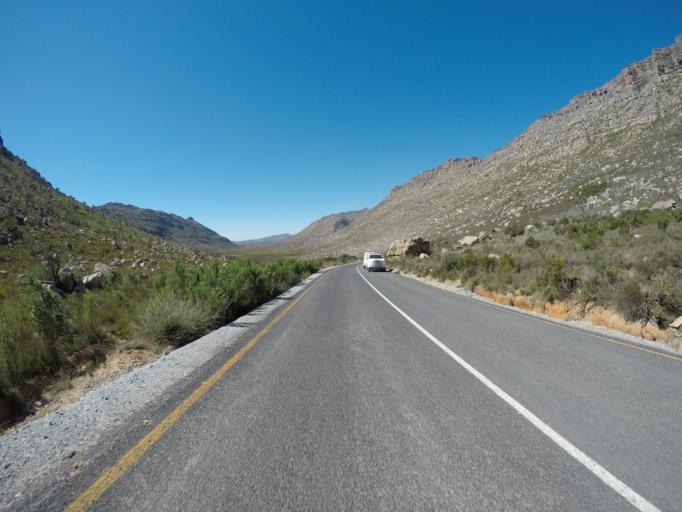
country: ZA
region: Western Cape
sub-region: West Coast District Municipality
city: Clanwilliam
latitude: -32.4076
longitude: 19.1070
